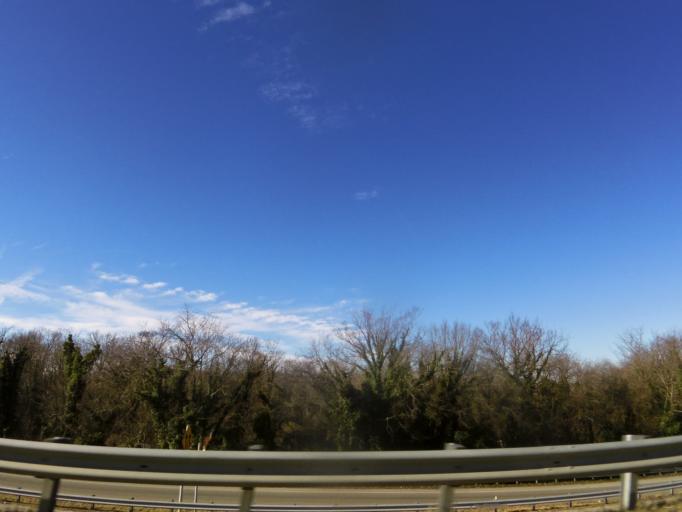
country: US
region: Virginia
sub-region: City of Petersburg
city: Petersburg
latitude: 37.2266
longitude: -77.3949
